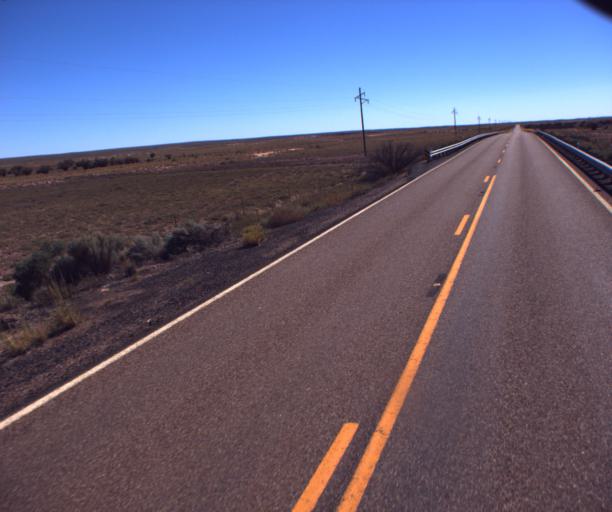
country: US
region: Arizona
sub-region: Navajo County
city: Holbrook
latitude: 35.0885
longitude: -110.0976
